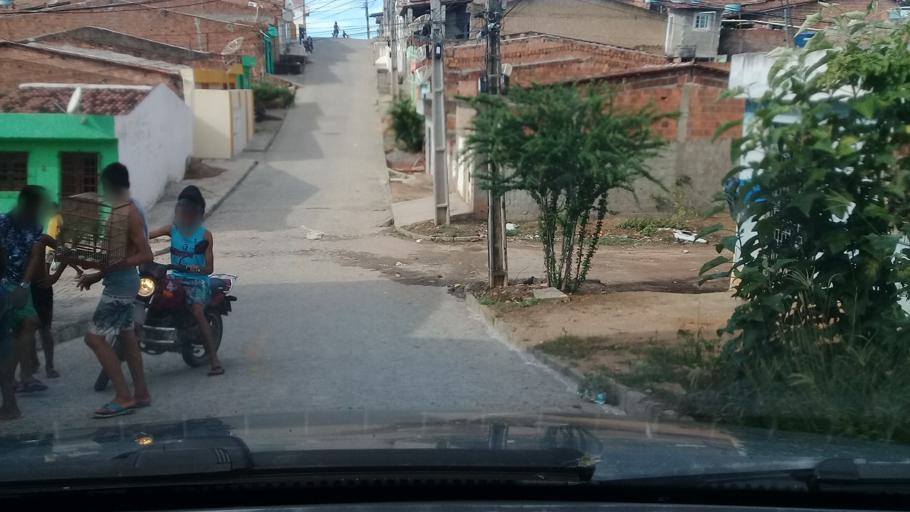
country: BR
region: Pernambuco
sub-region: Vitoria De Santo Antao
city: Vitoria de Santo Antao
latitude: -8.1285
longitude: -35.2886
